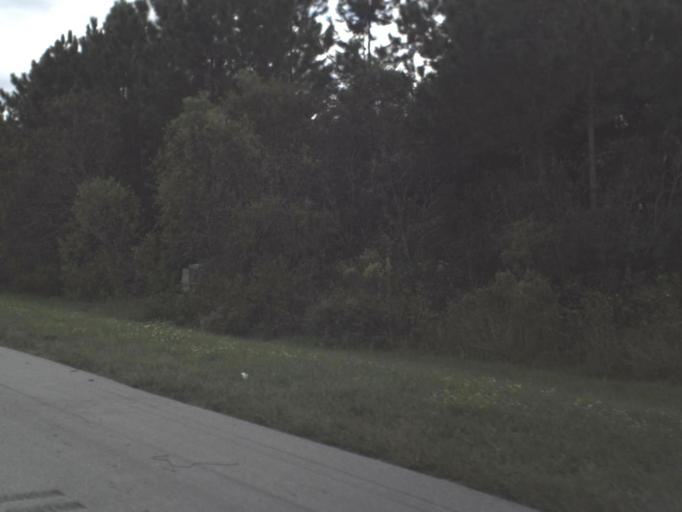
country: US
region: Florida
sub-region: Osceola County
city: Buenaventura Lakes
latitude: 28.3061
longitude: -81.3639
